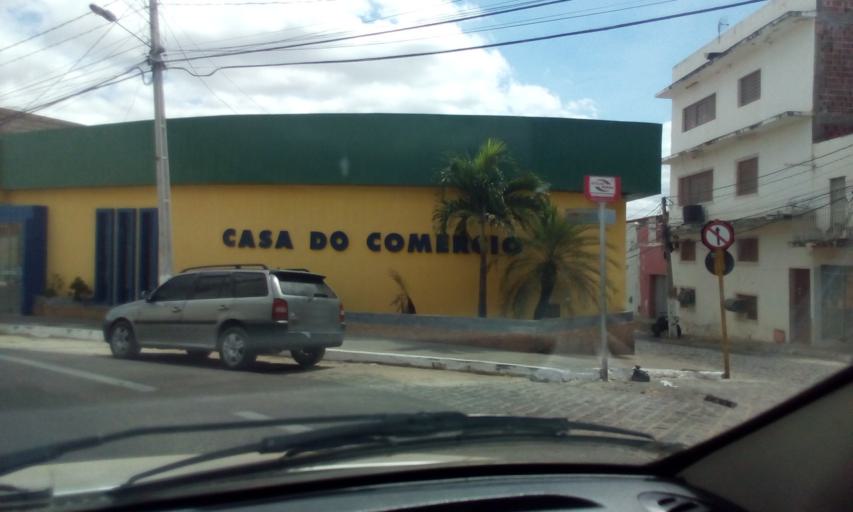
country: BR
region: Rio Grande do Norte
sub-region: Currais Novos
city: Currais Novos
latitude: -6.2625
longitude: -36.5170
